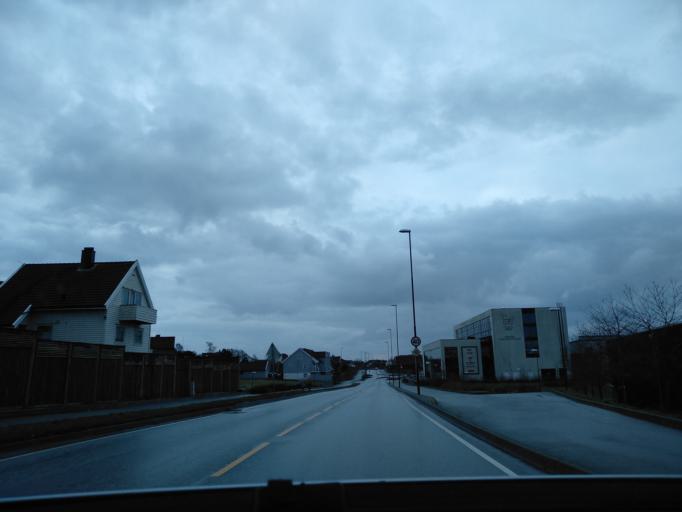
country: NO
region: Rogaland
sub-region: Stavanger
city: Stavanger
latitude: 58.9857
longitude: 5.6932
